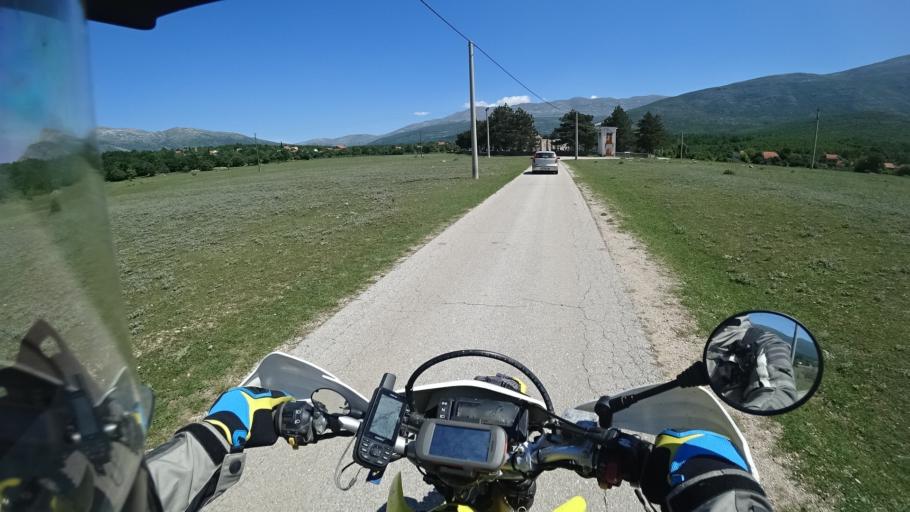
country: BA
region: Federation of Bosnia and Herzegovina
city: Bosansko Grahovo
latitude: 43.9721
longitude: 16.4258
